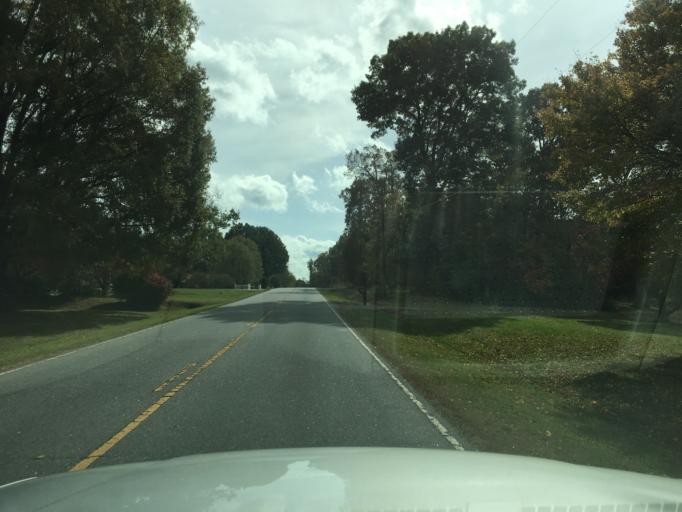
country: US
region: North Carolina
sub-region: Catawba County
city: Newton
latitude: 35.6716
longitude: -81.2731
